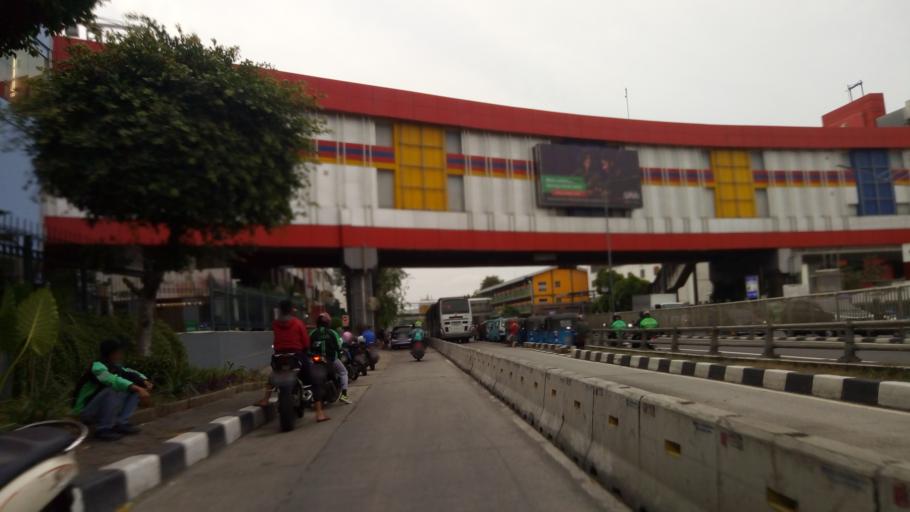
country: ID
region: Jakarta Raya
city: Jakarta
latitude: -6.1763
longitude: 106.8415
